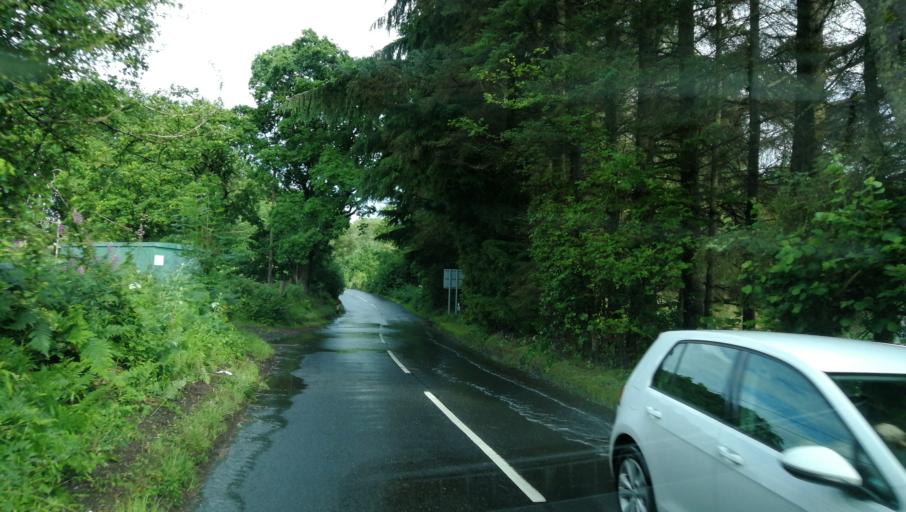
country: GB
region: Scotland
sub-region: Stirling
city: Callander
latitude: 56.2262
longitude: -4.3068
